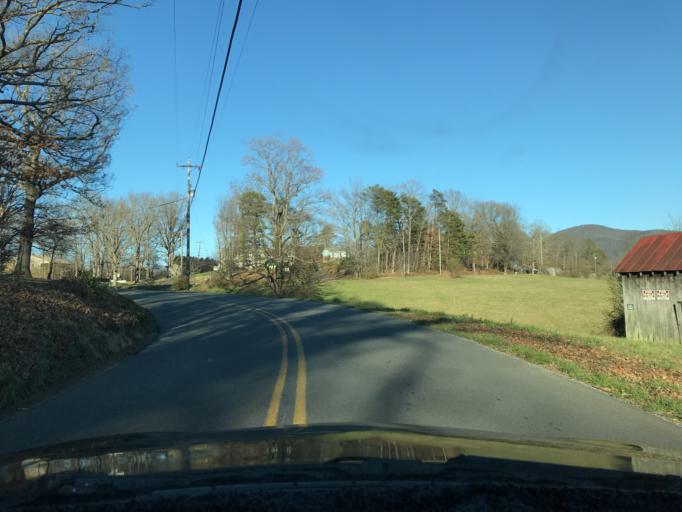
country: US
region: Virginia
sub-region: Botetourt County
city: Blue Ridge
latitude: 37.3896
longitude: -79.7202
